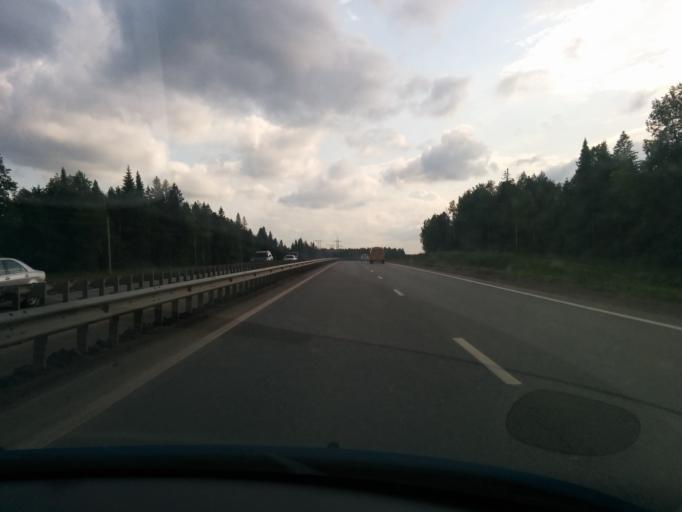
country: RU
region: Perm
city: Ferma
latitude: 58.0200
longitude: 56.4172
